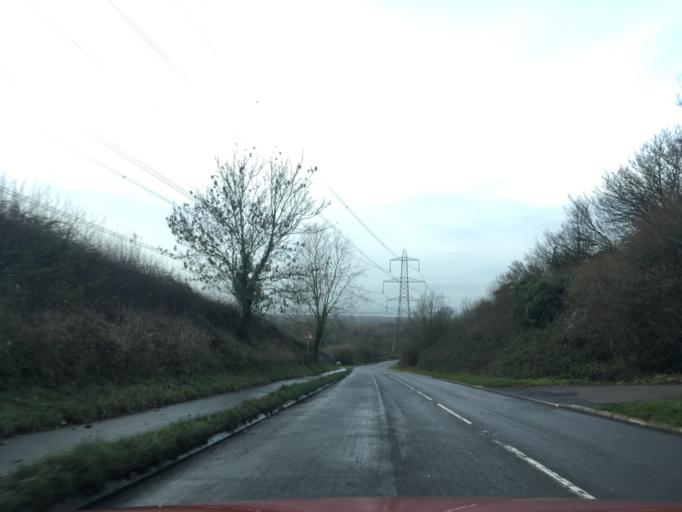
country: GB
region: England
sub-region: South Gloucestershire
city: Almondsbury
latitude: 51.5636
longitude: -2.5584
